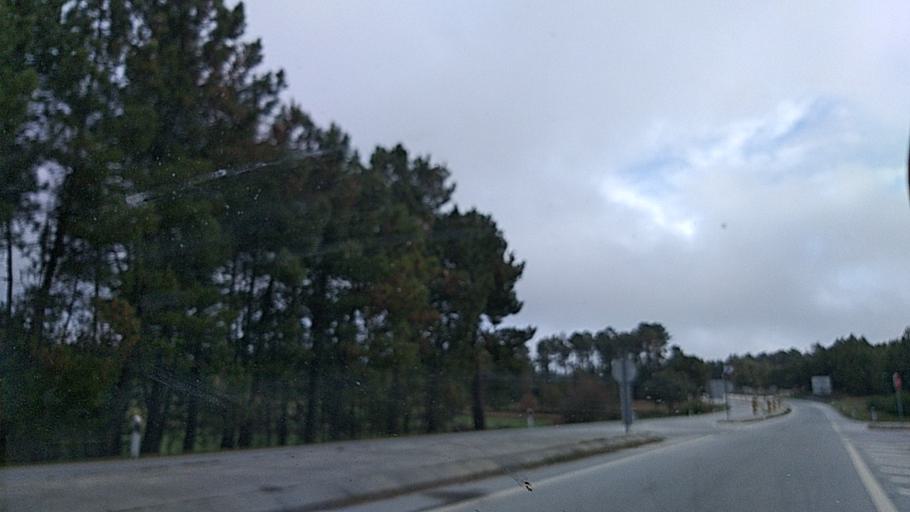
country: PT
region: Guarda
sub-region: Aguiar da Beira
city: Aguiar da Beira
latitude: 40.7313
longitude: -7.4950
